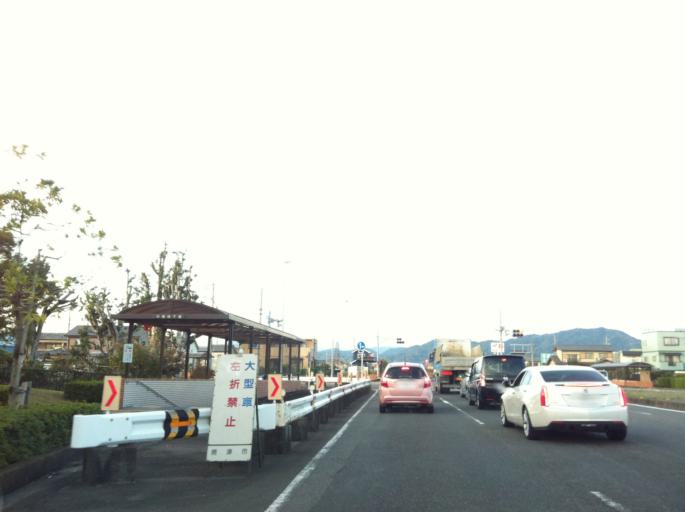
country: JP
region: Shizuoka
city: Yaizu
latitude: 34.8416
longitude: 138.3000
